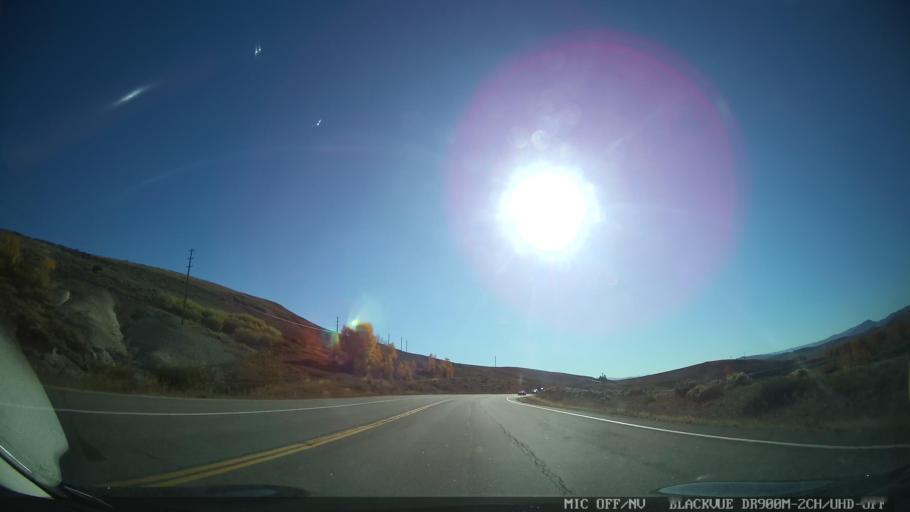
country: US
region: Colorado
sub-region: Grand County
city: Granby
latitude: 40.1079
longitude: -105.9780
